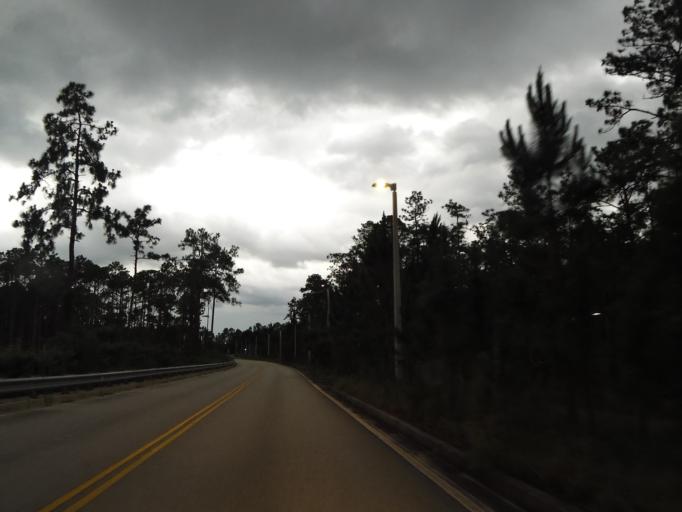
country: US
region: Florida
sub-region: Duval County
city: Jacksonville Beach
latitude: 30.2735
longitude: -81.5139
